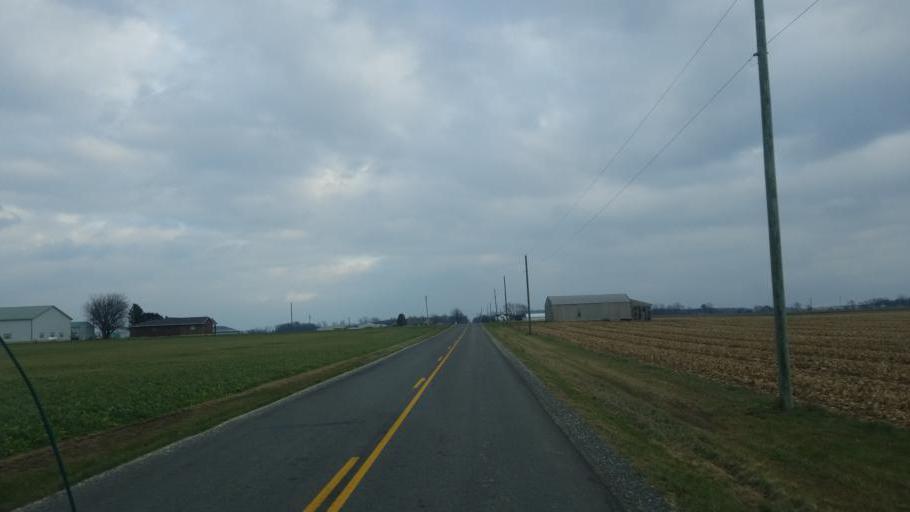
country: US
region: Ohio
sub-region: Mercer County
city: Coldwater
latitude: 40.5090
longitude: -84.6712
